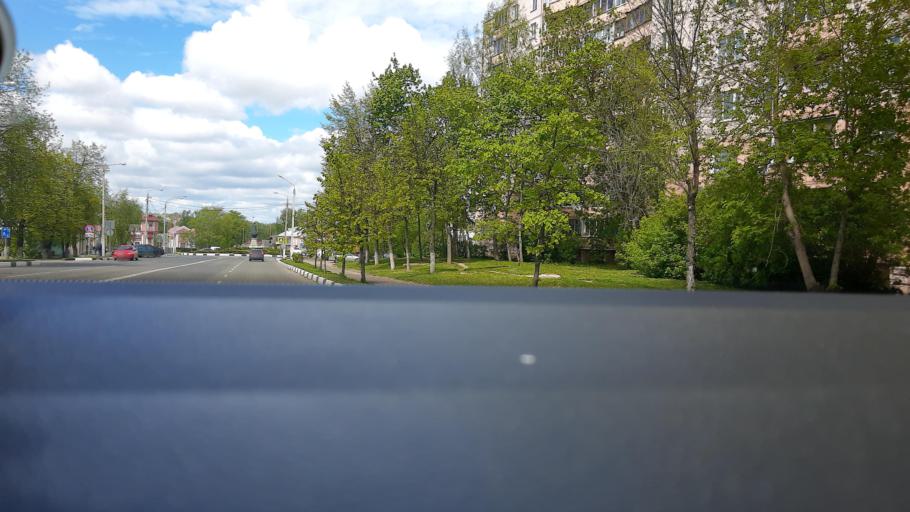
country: RU
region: Moskovskaya
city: Dmitrov
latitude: 56.3364
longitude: 37.5161
